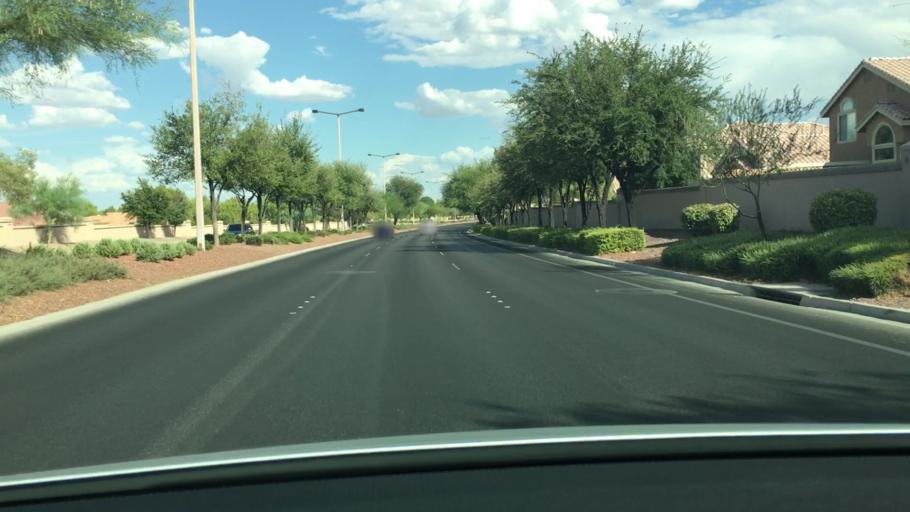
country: US
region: Nevada
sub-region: Clark County
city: Summerlin South
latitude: 36.2053
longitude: -115.2943
